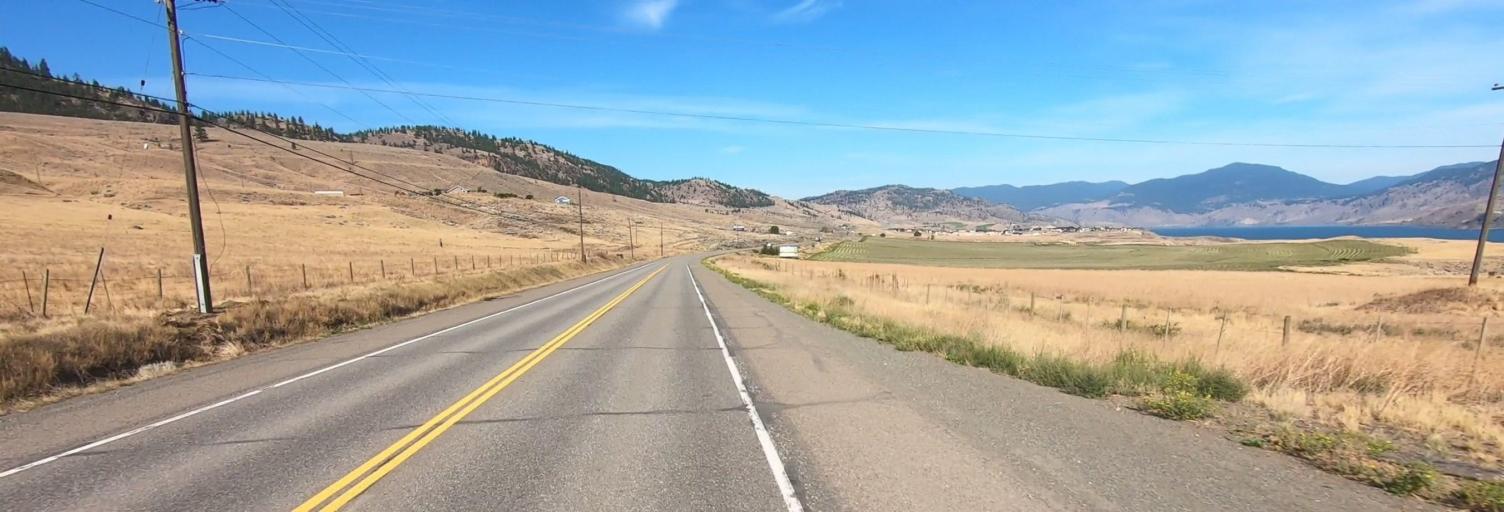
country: CA
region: British Columbia
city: Logan Lake
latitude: 50.7185
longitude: -120.6482
